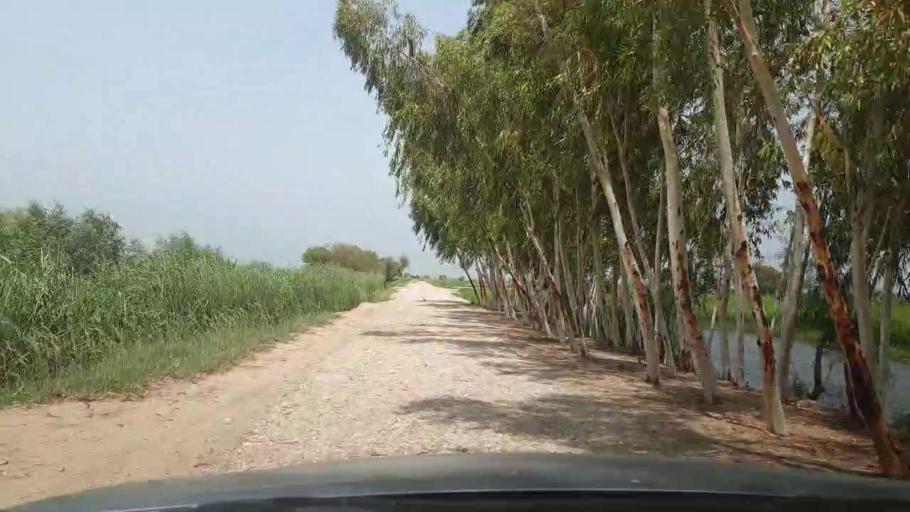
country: PK
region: Sindh
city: Garhi Yasin
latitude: 27.9239
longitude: 68.4337
